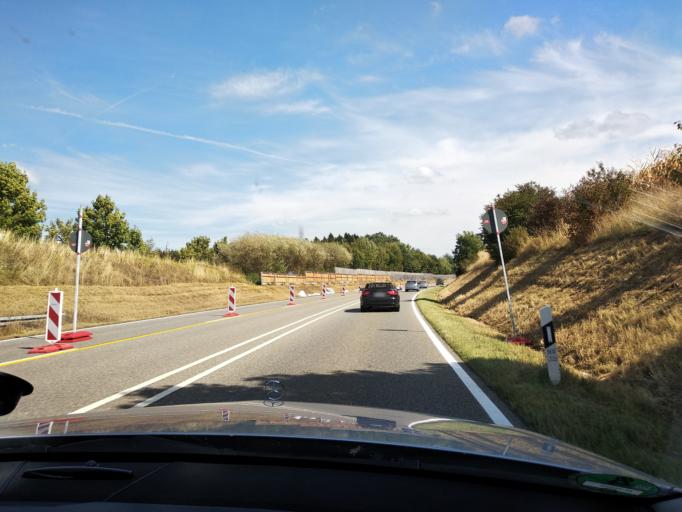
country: DE
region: Baden-Wuerttemberg
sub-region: Tuebingen Region
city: Amtzell
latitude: 47.6991
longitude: 9.7510
